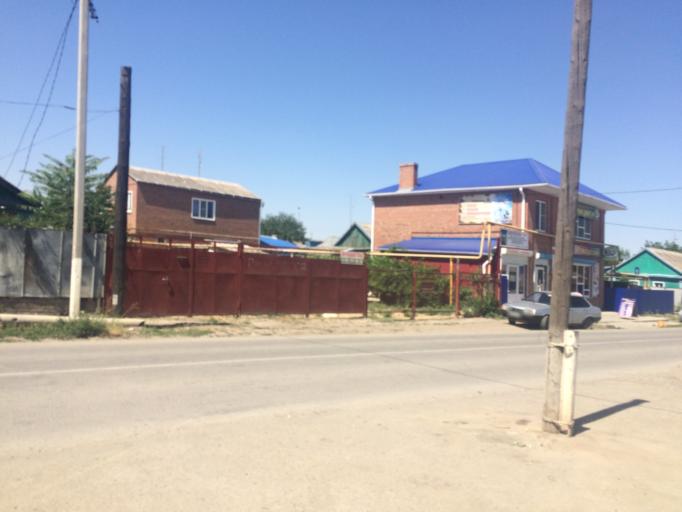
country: RU
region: Rostov
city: Sal'sk
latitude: 46.4692
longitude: 41.5358
